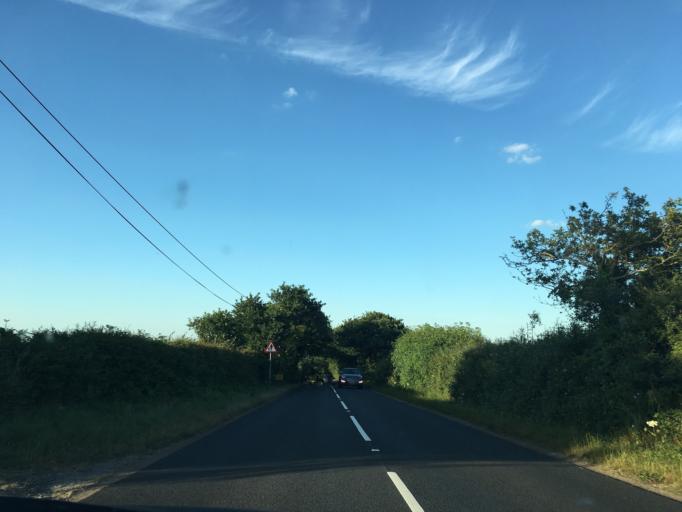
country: GB
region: England
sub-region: Isle of Wight
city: Newport
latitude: 50.7088
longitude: -1.2585
